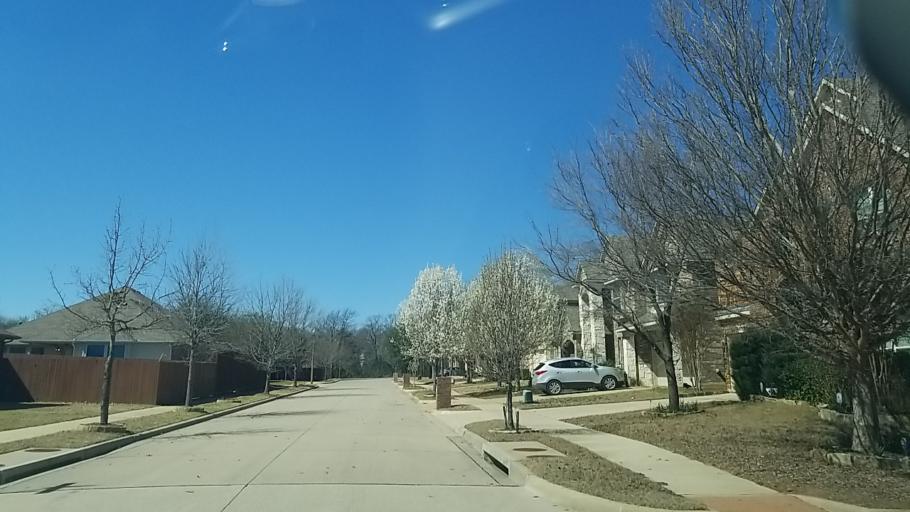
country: US
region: Texas
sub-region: Denton County
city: Corinth
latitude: 33.1574
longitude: -97.1082
